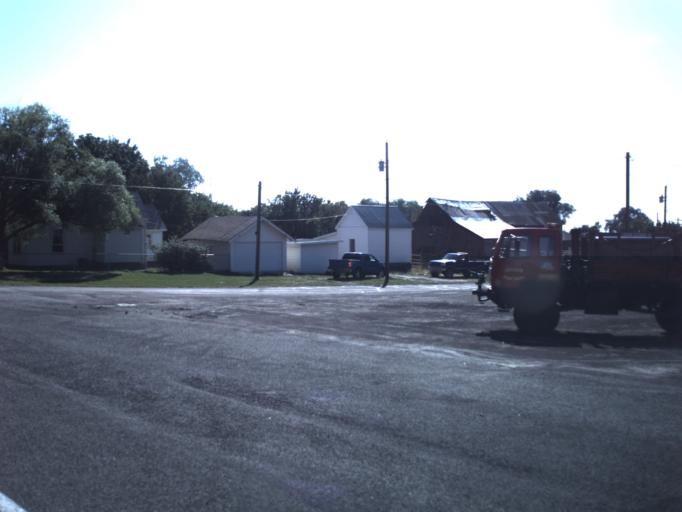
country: US
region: Utah
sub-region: Millard County
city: Fillmore
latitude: 39.0981
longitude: -112.2709
